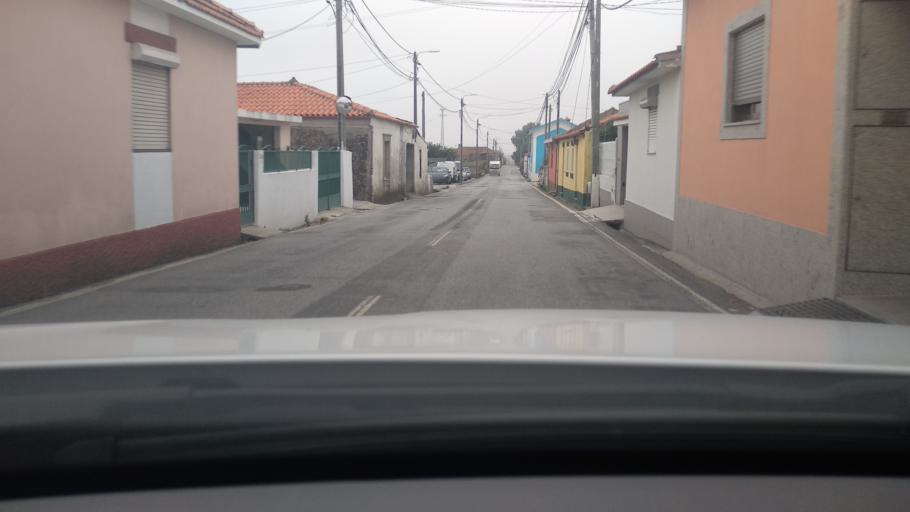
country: PT
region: Aveiro
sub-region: Espinho
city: Souto
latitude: 40.9857
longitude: -8.6238
